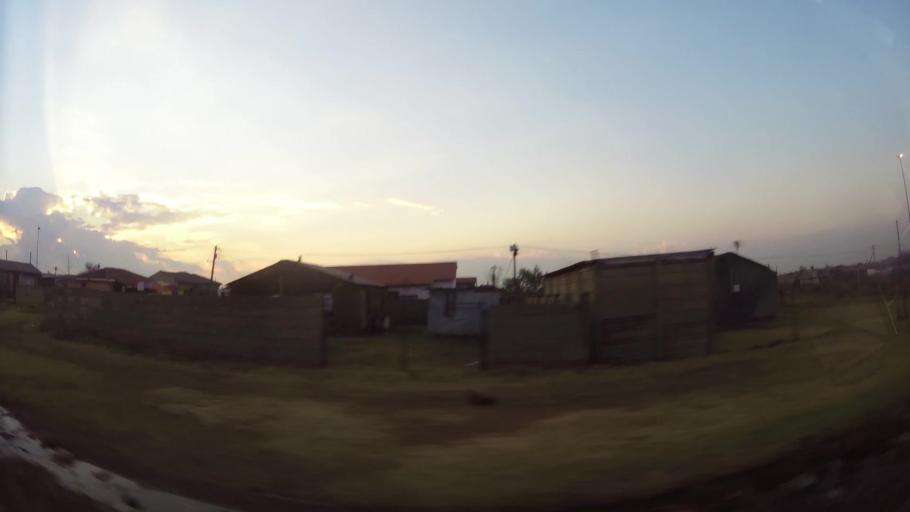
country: ZA
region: Gauteng
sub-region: City of Johannesburg Metropolitan Municipality
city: Orange Farm
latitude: -26.5531
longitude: 27.8712
